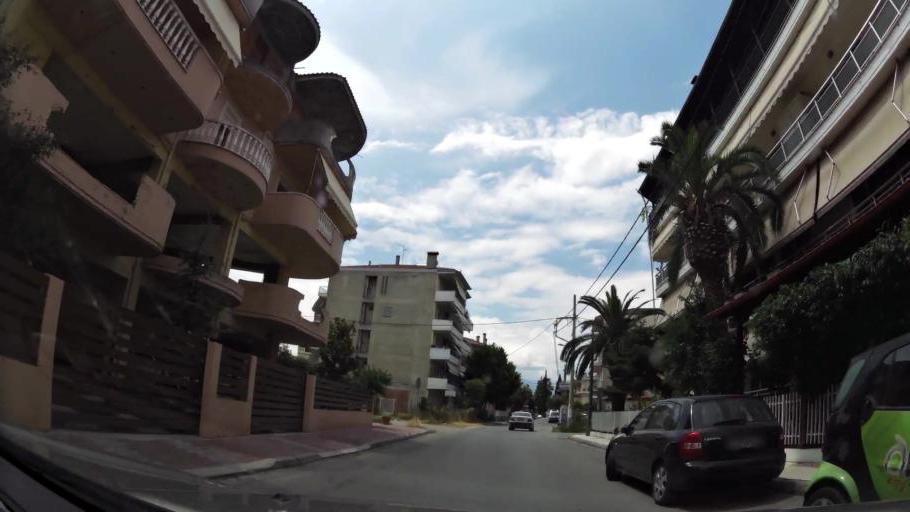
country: GR
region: Central Macedonia
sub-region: Nomos Pierias
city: Katerini
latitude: 40.2668
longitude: 22.5157
